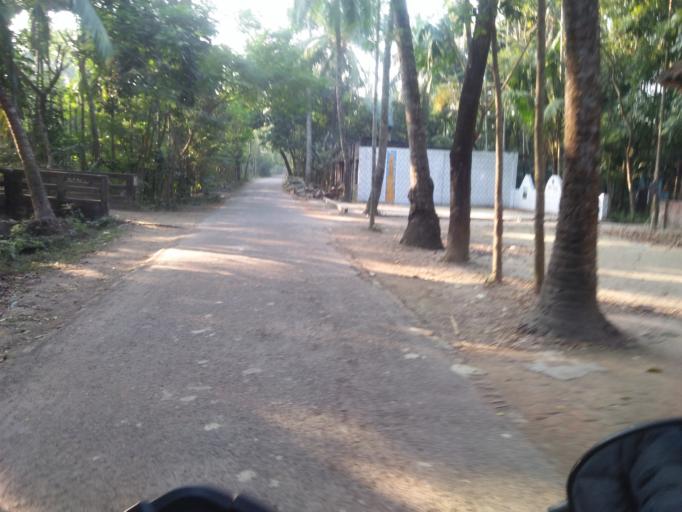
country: BD
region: Barisal
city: Bhola
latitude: 22.7526
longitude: 90.6318
